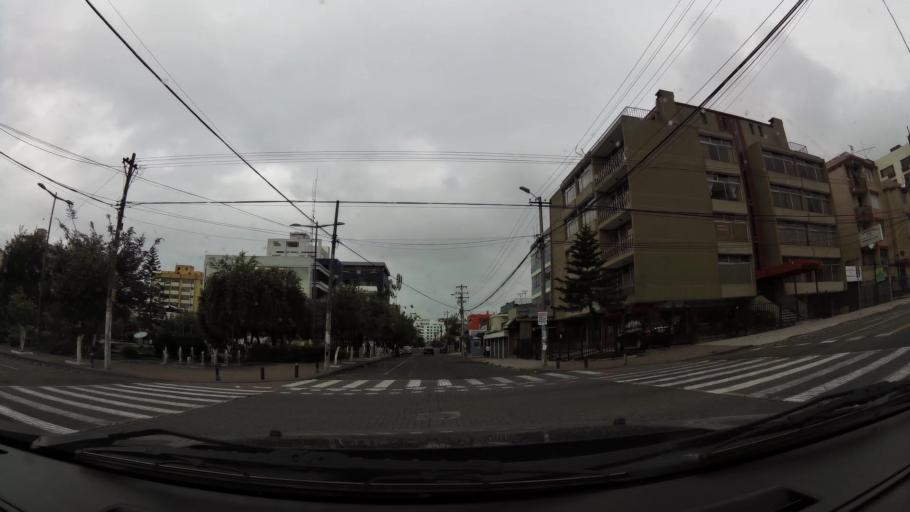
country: EC
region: Pichincha
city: Quito
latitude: -0.1891
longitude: -78.4904
